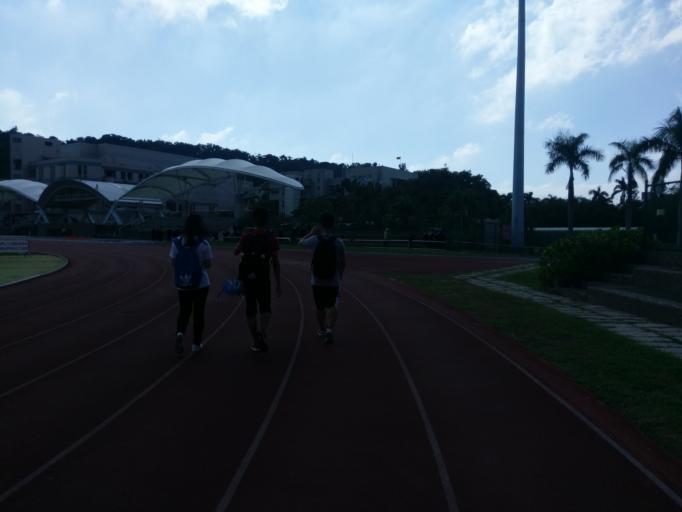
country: TW
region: Taiwan
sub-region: Changhua
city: Chang-hua
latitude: 24.0824
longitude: 120.5601
